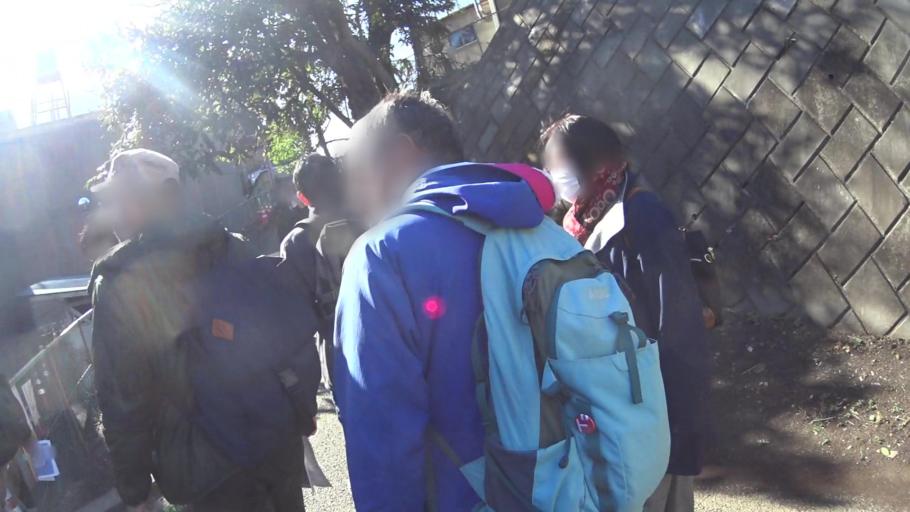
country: JP
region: Saitama
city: Yono
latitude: 35.8551
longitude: 139.6505
